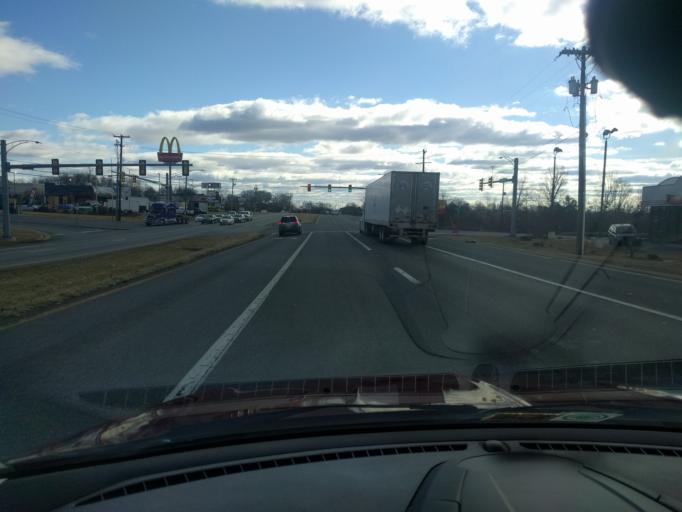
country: US
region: Virginia
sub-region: City of Bedford
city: Bedford
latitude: 37.3238
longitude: -79.4979
